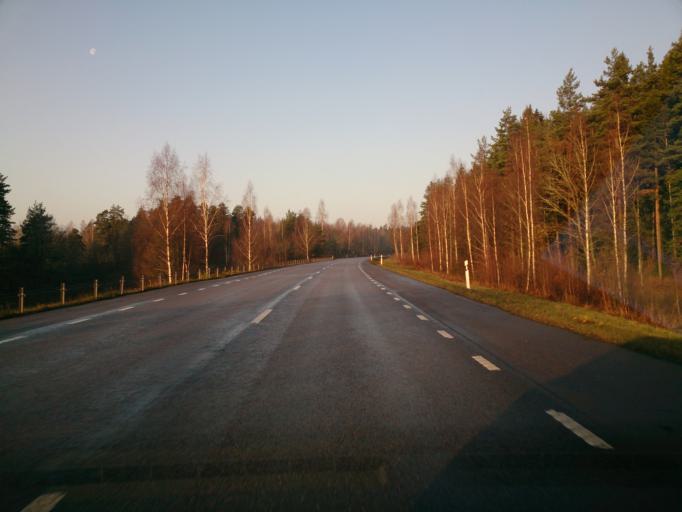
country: SE
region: OEstergoetland
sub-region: Atvidabergs Kommun
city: Atvidaberg
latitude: 58.2365
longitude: 15.9472
